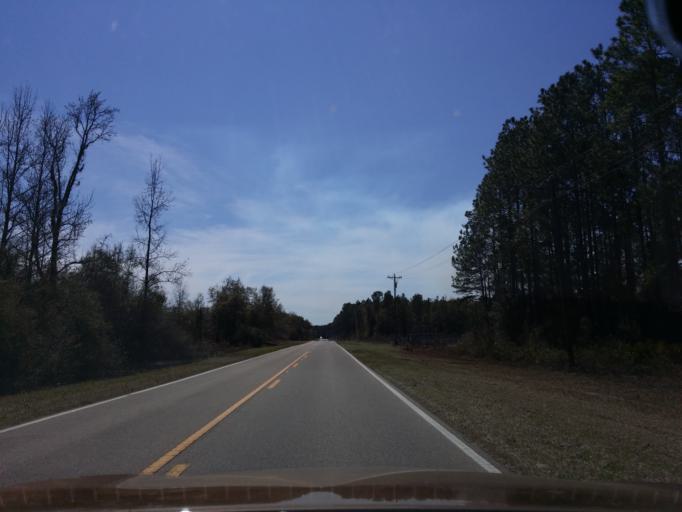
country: US
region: Florida
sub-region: Leon County
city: Woodville
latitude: 30.3512
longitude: -84.1351
